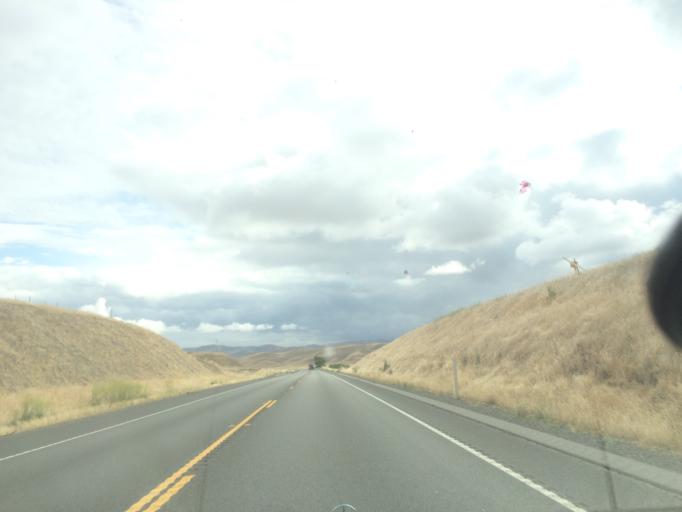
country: US
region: California
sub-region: San Luis Obispo County
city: Shandon
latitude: 35.7144
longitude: -120.3049
